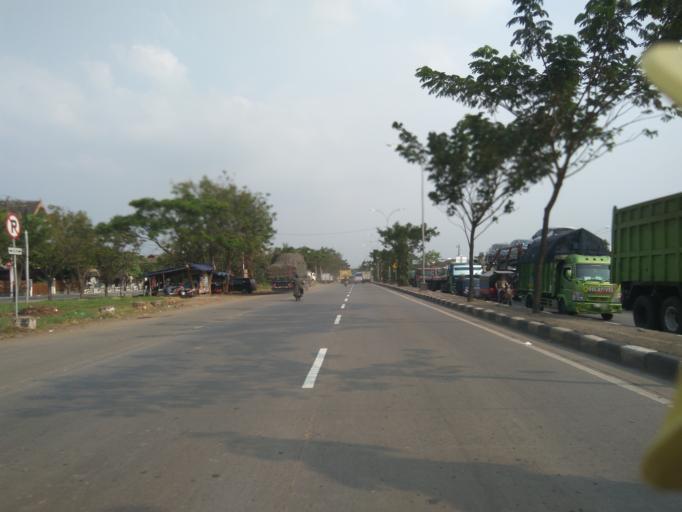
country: ID
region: Central Java
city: Semarang
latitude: -6.9627
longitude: 110.3941
